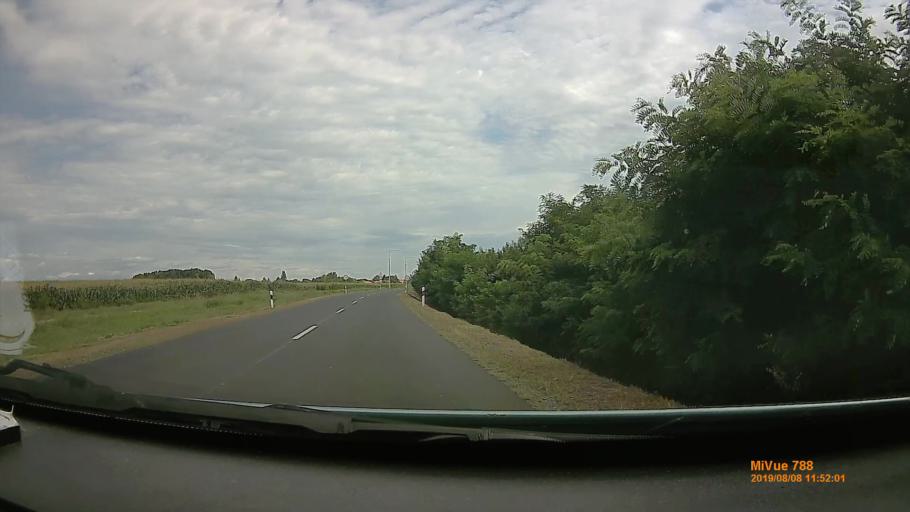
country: HU
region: Szabolcs-Szatmar-Bereg
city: Nyirmihalydi
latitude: 47.7258
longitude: 21.9507
